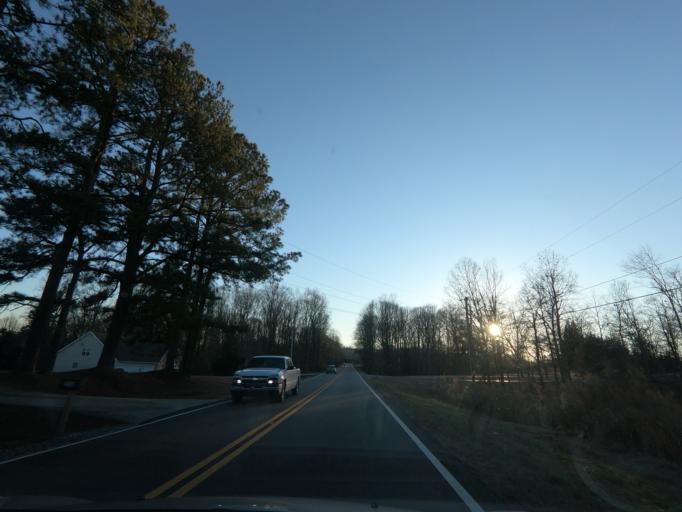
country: US
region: Georgia
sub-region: Dawson County
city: Dawsonville
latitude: 34.3289
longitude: -84.1289
